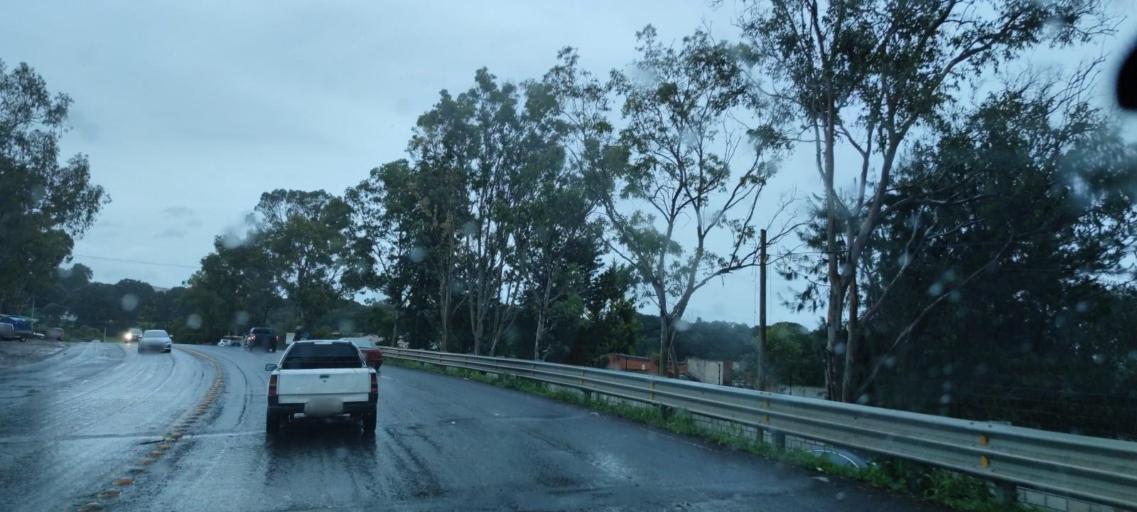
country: MX
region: Mexico
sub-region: Jilotepec
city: Doxhicho
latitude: 19.9355
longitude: -99.5671
